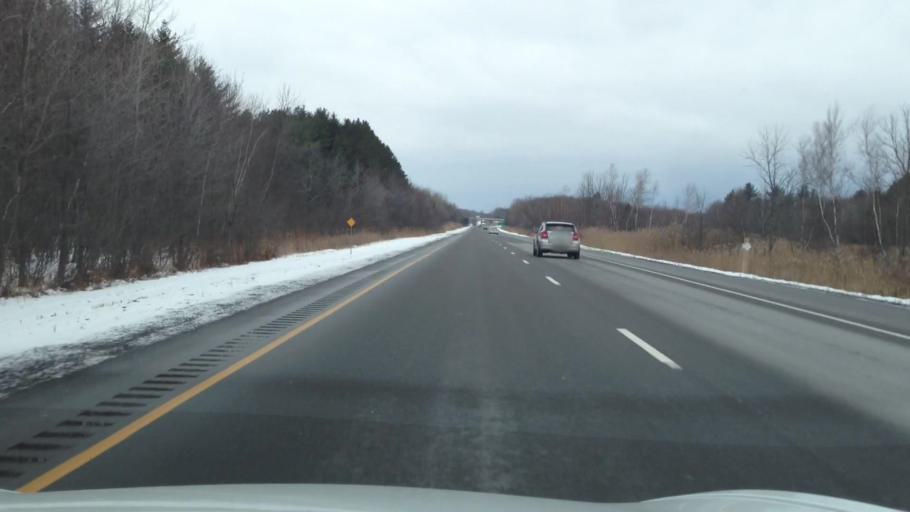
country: CA
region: Quebec
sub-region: Laurentides
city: Brownsburg-Chatham
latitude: 45.5501
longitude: -74.4345
